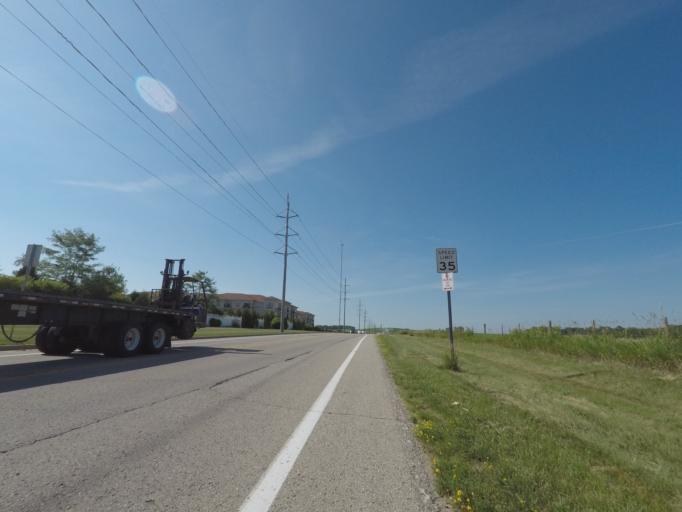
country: US
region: Wisconsin
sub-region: Dane County
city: Middleton
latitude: 43.0702
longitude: -89.5372
